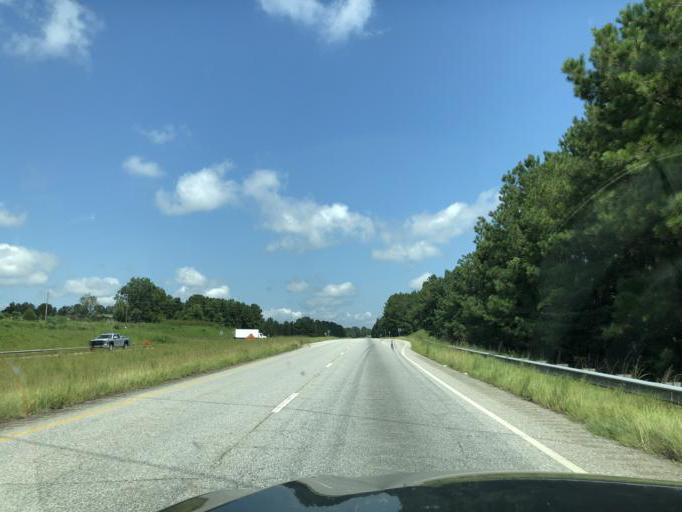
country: US
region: Alabama
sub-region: Henry County
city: Abbeville
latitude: 31.6877
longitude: -85.2788
